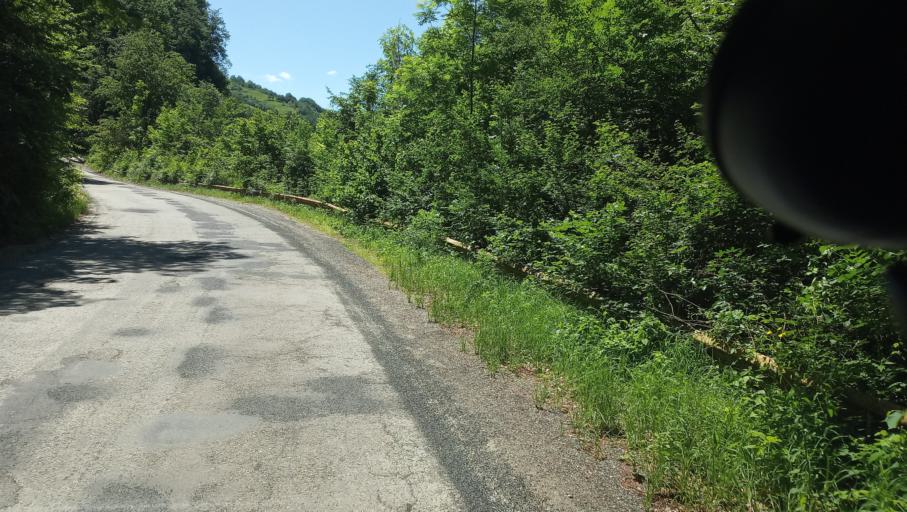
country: RO
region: Mehedinti
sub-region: Comuna Isverna
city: Isverna
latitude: 45.0010
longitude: 22.5345
